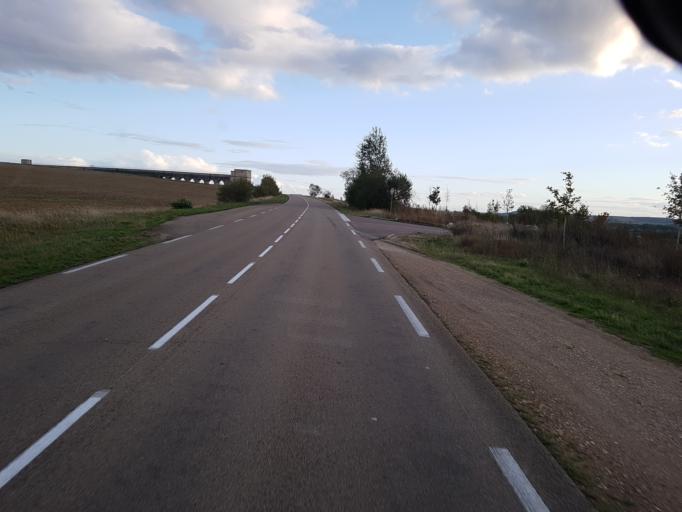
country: FR
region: Bourgogne
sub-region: Departement de l'Yonne
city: Soucy
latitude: 48.2755
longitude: 3.2723
